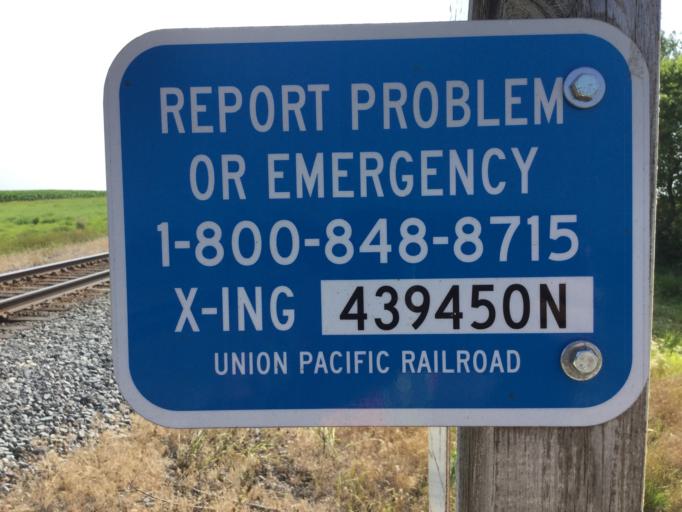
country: US
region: Kansas
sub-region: Anderson County
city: Garnett
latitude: 38.2108
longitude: -95.4069
